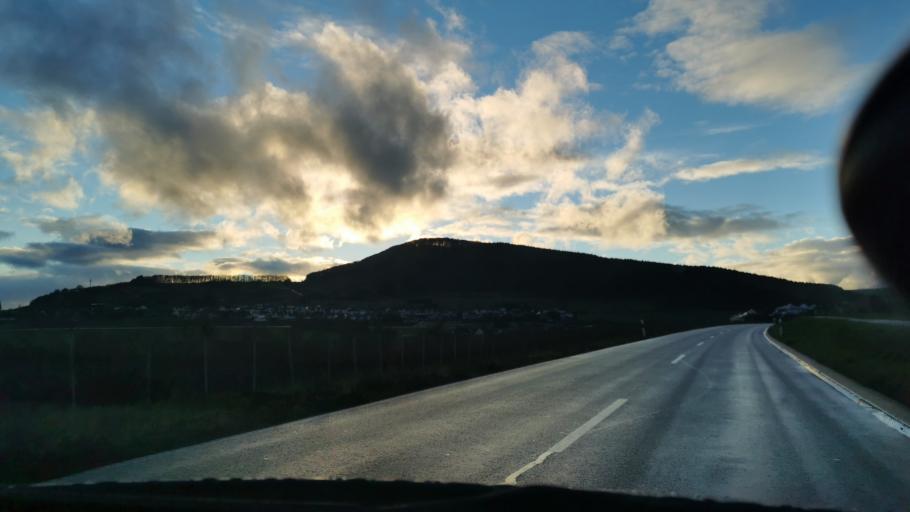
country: DE
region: Rheinland-Pfalz
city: Osann-Monzel
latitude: 49.9206
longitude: 6.9648
